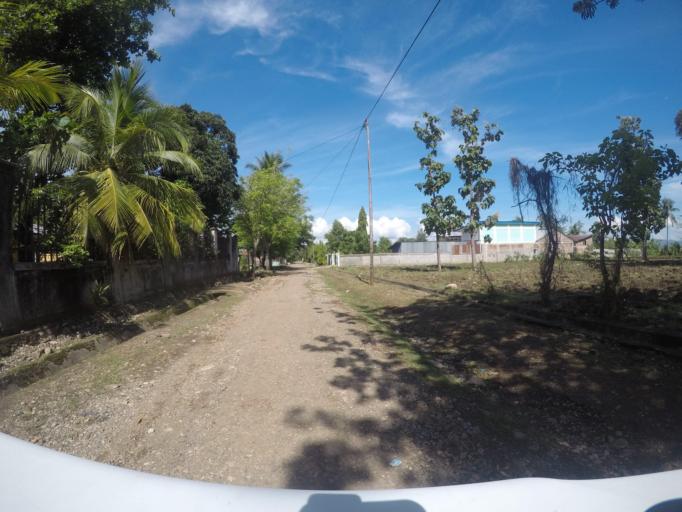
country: TL
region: Bobonaro
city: Maliana
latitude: -8.9878
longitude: 125.2025
